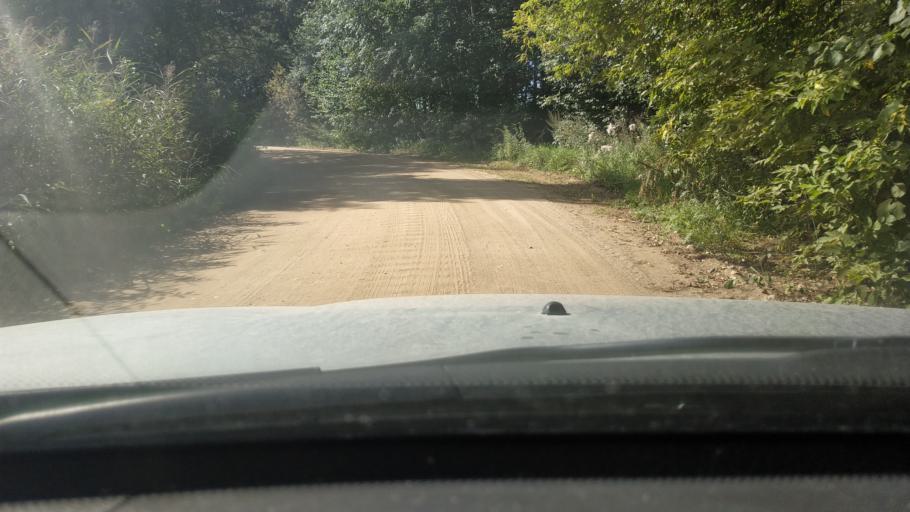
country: RU
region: Kostroma
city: Kosmynino
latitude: 57.7744
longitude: 40.7307
